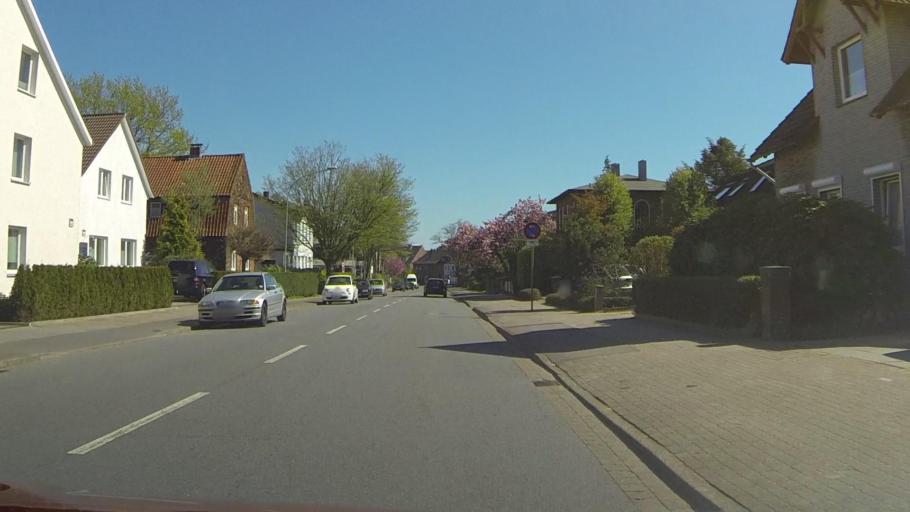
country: DE
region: Schleswig-Holstein
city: Pinneberg
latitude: 53.6664
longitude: 9.7879
